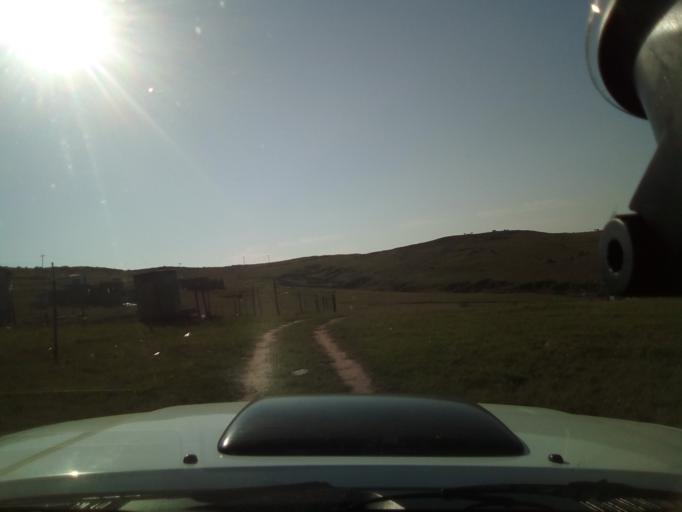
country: ZA
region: Eastern Cape
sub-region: Buffalo City Metropolitan Municipality
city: East London
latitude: -32.8410
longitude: 27.9960
